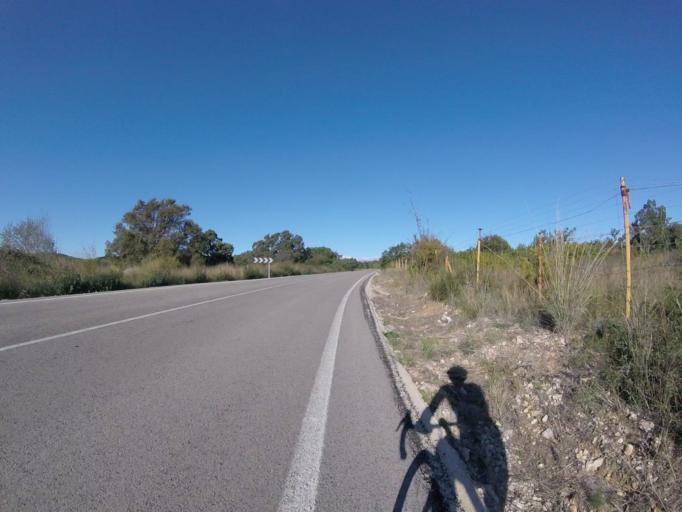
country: ES
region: Valencia
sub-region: Provincia de Castello
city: Cervera del Maestre
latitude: 40.4738
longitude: 0.2316
